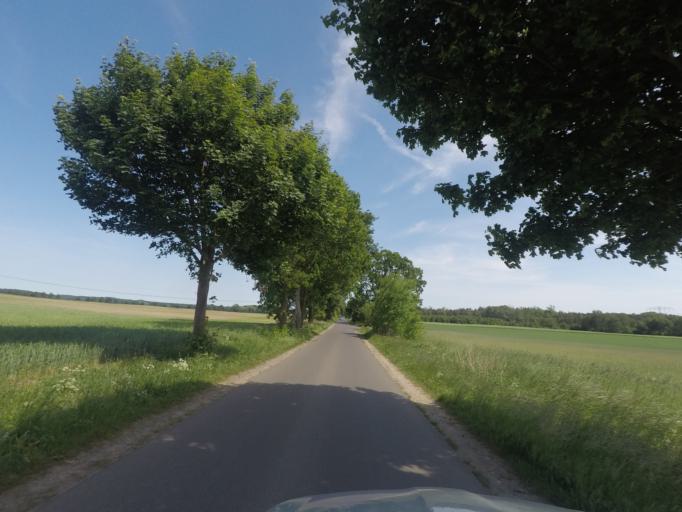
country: DE
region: Brandenburg
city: Britz
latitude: 52.8914
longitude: 13.7892
